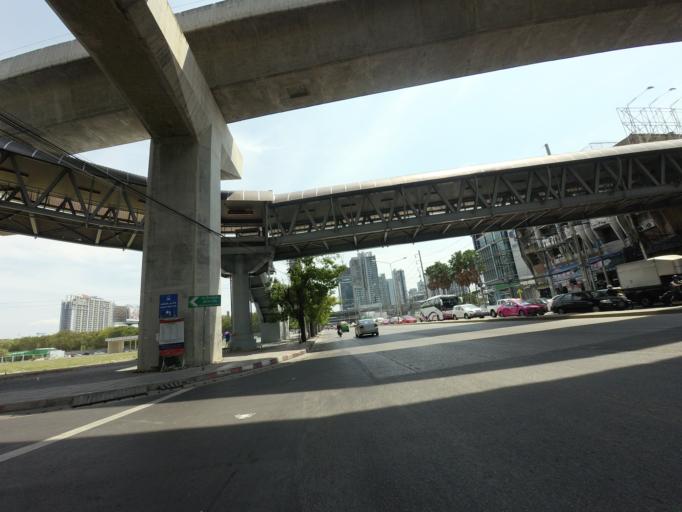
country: TH
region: Bangkok
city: Din Daeng
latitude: 13.7503
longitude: 100.5636
